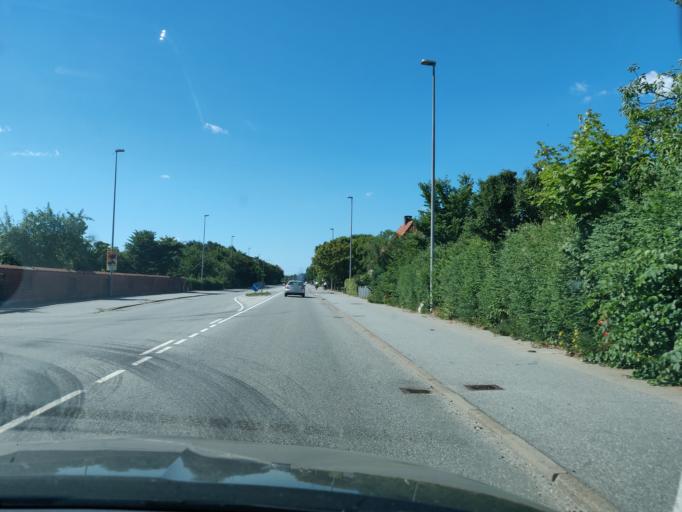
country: DK
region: North Denmark
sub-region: Alborg Kommune
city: Aalborg
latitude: 57.0734
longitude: 9.9499
